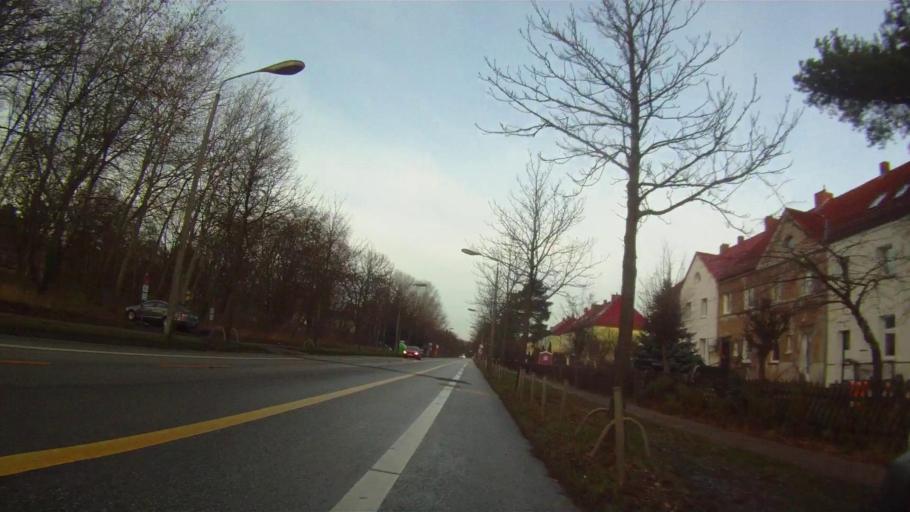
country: DE
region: Berlin
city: Johannisthal
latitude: 52.4556
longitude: 13.5027
